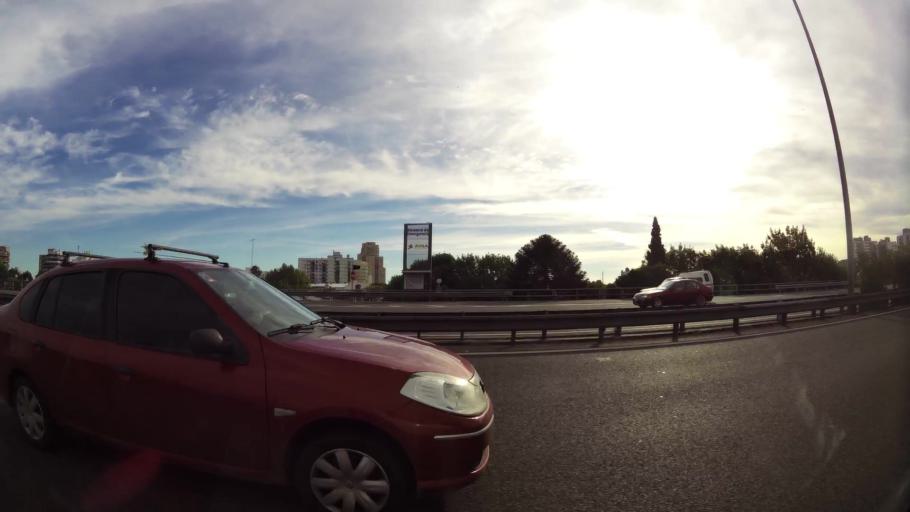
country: AR
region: Buenos Aires F.D.
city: Villa Santa Rita
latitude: -34.6407
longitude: -58.4923
